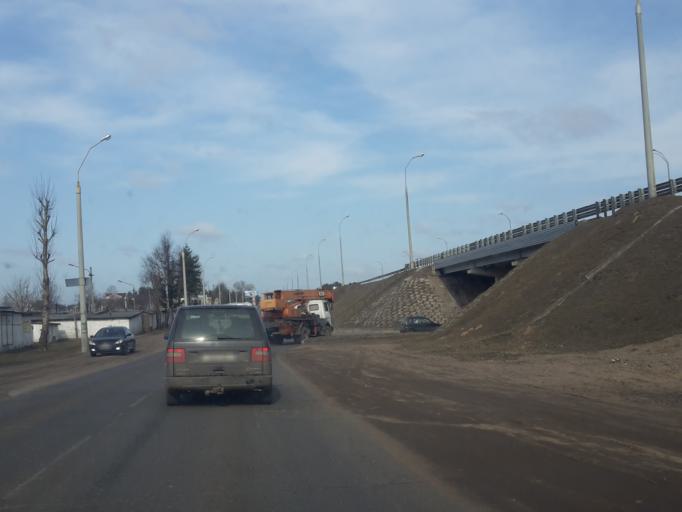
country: BY
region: Minsk
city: Vyaliki Trastsyanets
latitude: 53.9088
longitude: 27.6858
